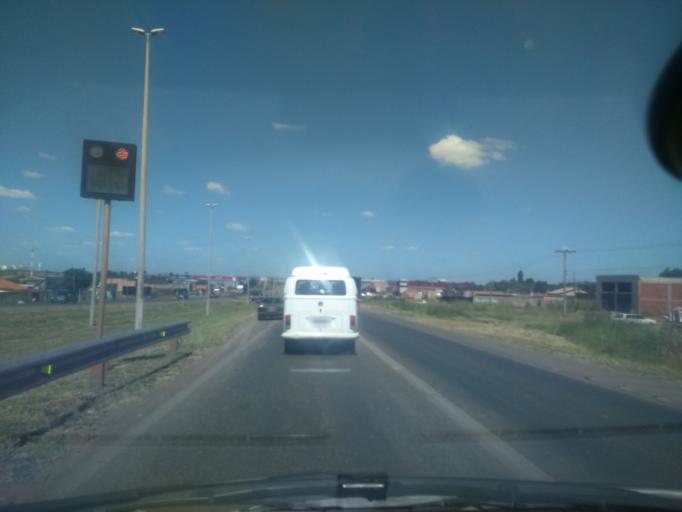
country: BR
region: Goias
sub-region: Luziania
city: Luziania
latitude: -16.1077
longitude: -47.9730
